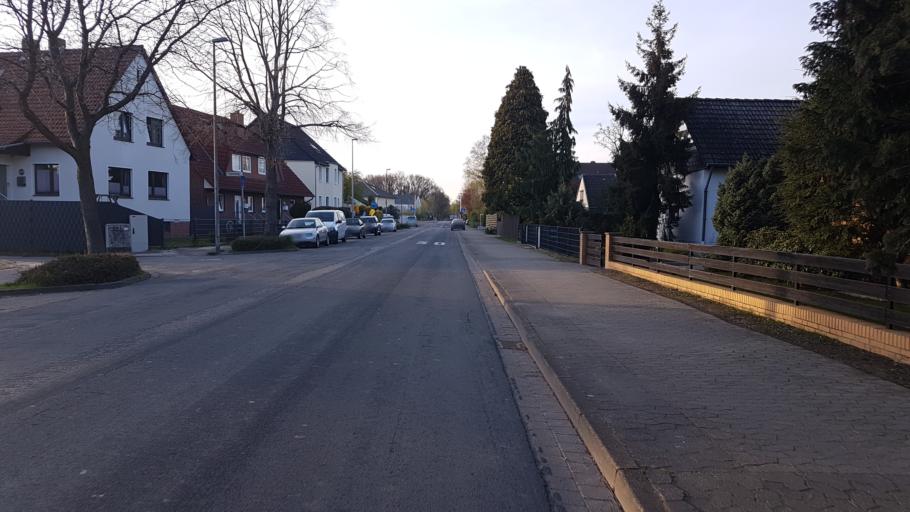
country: DE
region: Lower Saxony
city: Isernhagen Farster Bauerschaft
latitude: 52.4356
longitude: 9.8561
